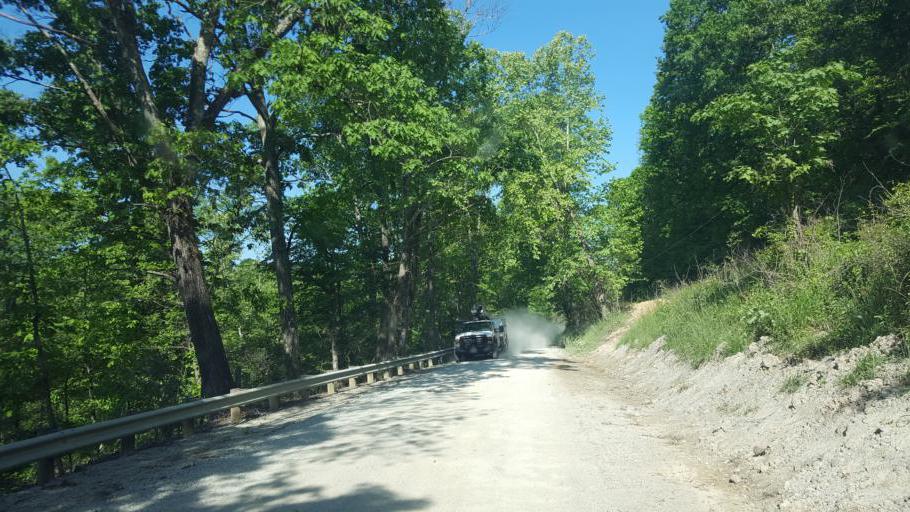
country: US
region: Ohio
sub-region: Jackson County
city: Wellston
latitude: 38.9936
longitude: -82.4263
